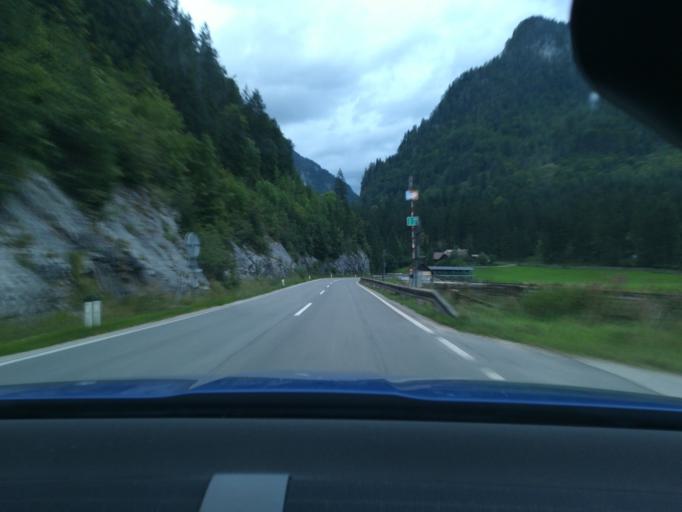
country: AT
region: Upper Austria
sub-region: Politischer Bezirk Gmunden
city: Bad Goisern
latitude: 47.5902
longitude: 13.5757
